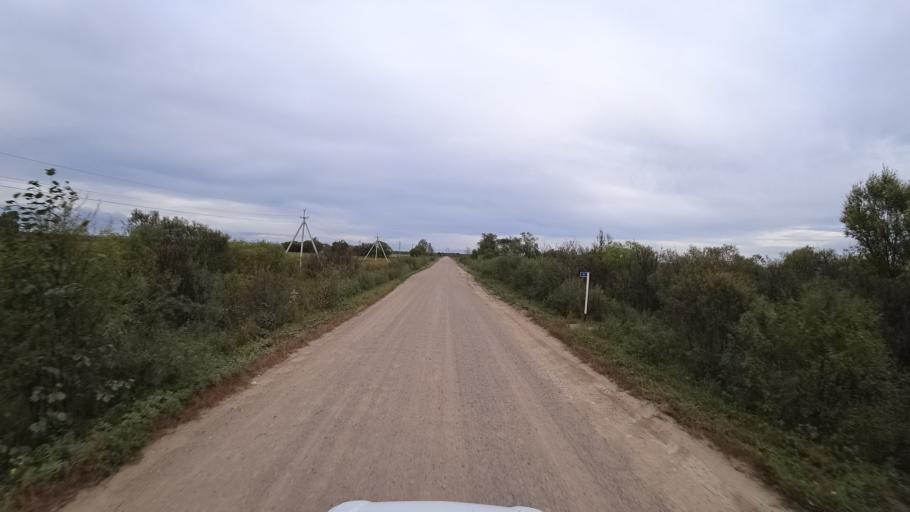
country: RU
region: Amur
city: Arkhara
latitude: 49.4309
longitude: 130.2344
